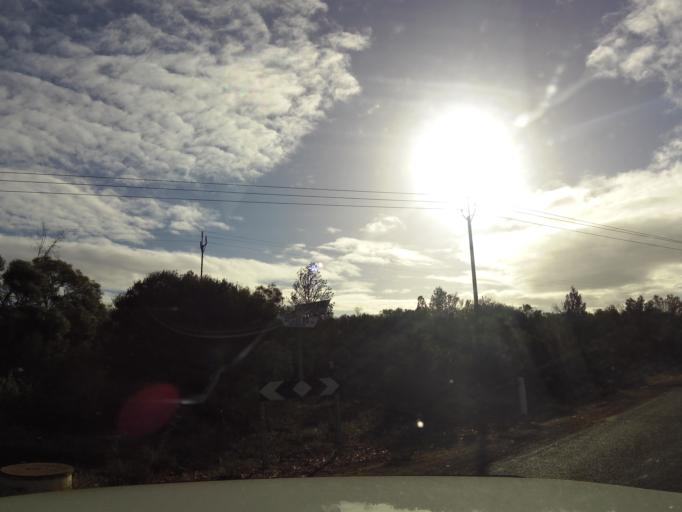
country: AU
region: South Australia
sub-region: Berri and Barmera
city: Berri
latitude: -34.2716
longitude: 140.5839
